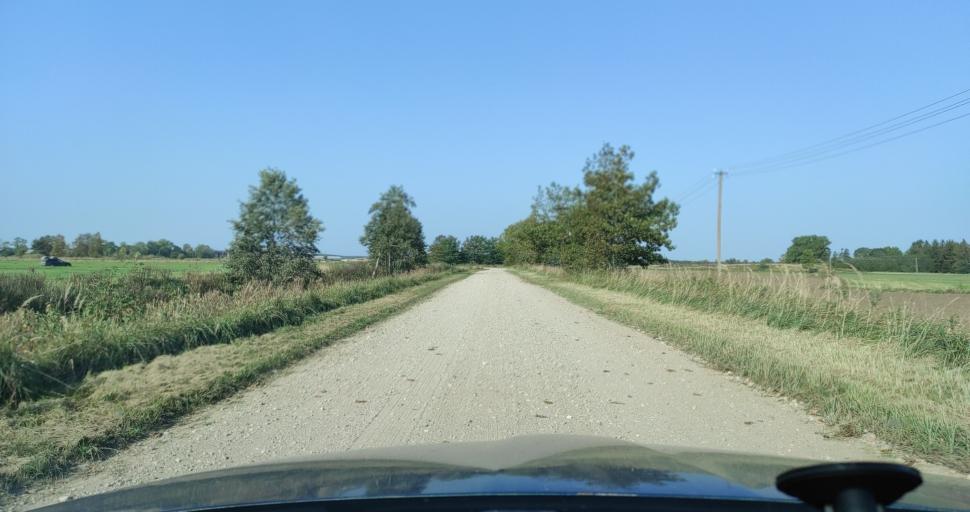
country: LV
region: Ventspils Rajons
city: Piltene
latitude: 57.2317
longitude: 21.6120
